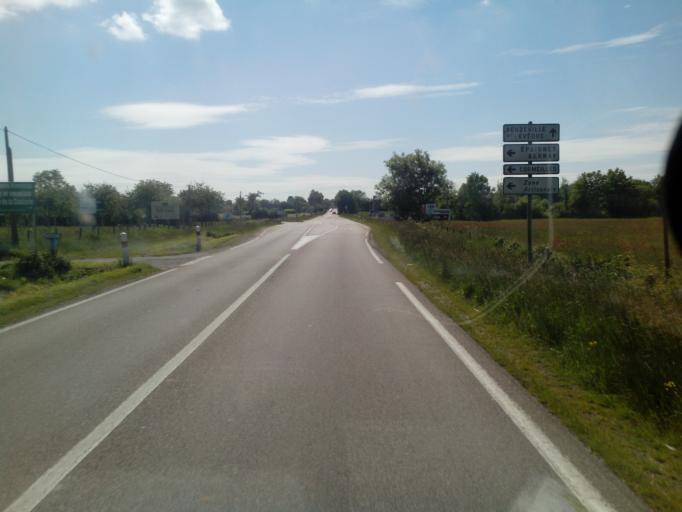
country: FR
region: Haute-Normandie
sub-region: Departement de l'Eure
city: Beuzeville
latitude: 49.3489
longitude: 0.3639
